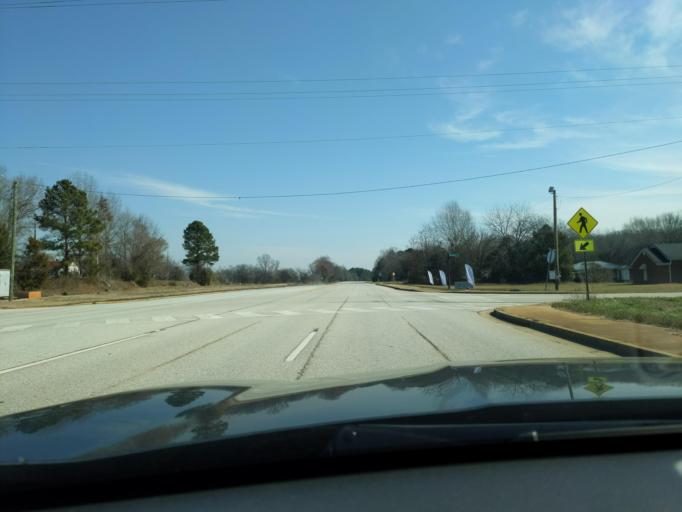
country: US
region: South Carolina
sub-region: Abbeville County
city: Calhoun Falls
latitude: 34.0956
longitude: -82.5868
